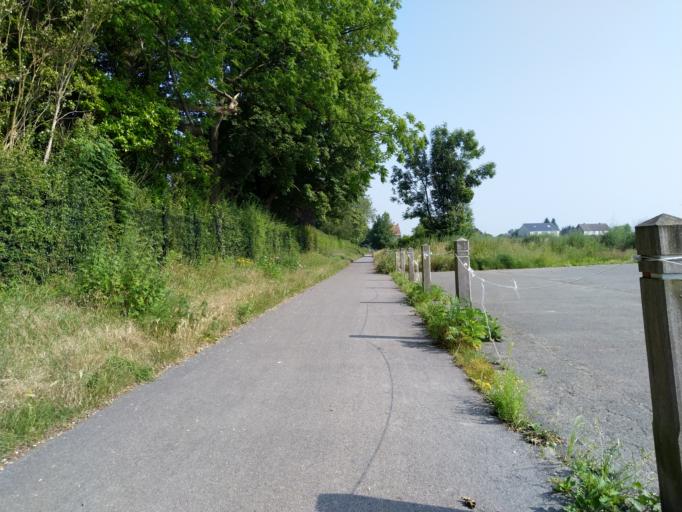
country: BE
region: Wallonia
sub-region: Province du Hainaut
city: Soignies
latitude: 50.5655
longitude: 3.9993
